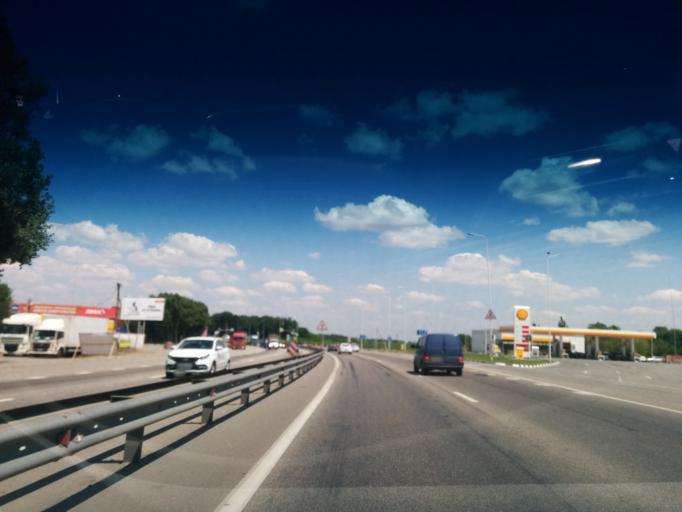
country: RU
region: Rostov
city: Aksay
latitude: 47.2994
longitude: 39.8617
